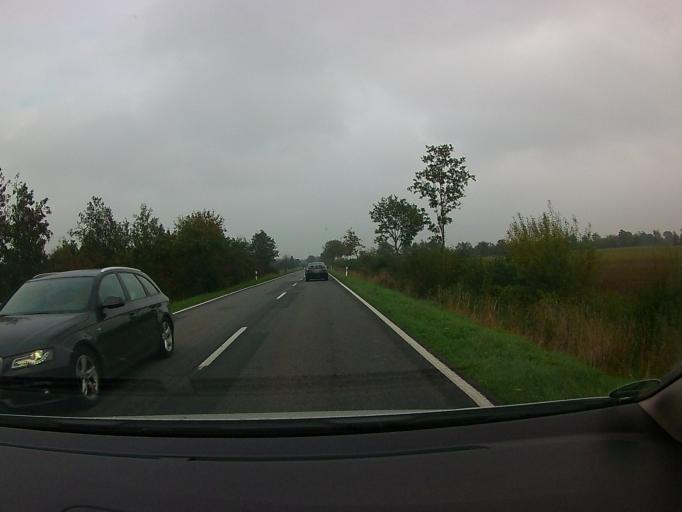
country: DE
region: Schleswig-Holstein
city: Wanderup
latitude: 54.6971
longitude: 9.3061
